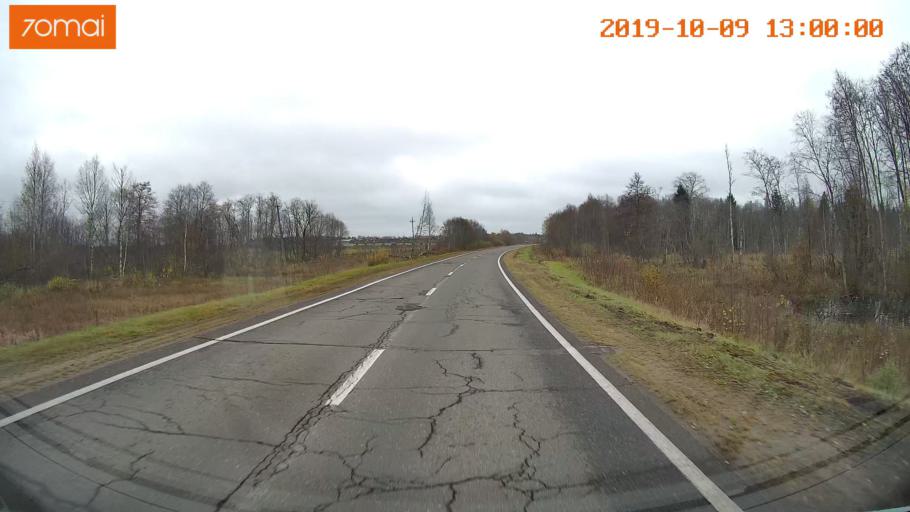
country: RU
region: Jaroslavl
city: Prechistoye
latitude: 58.3808
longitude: 40.4741
